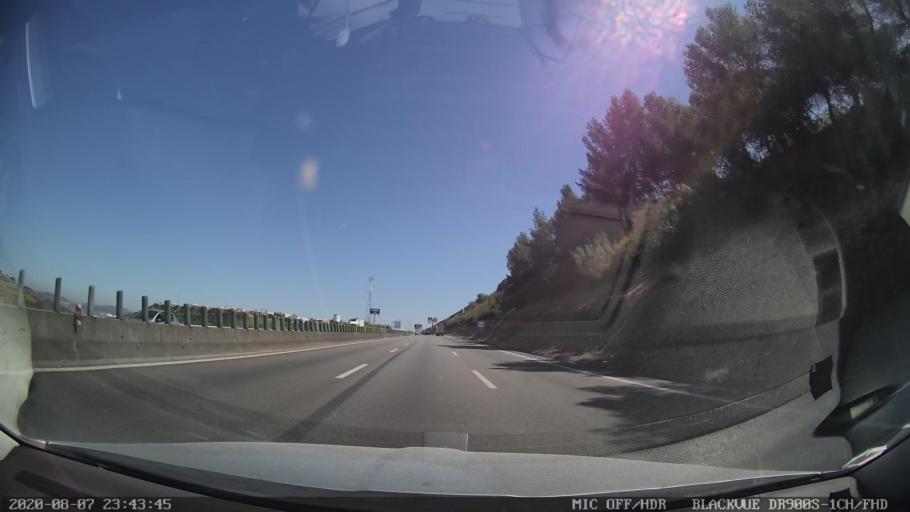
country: PT
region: Lisbon
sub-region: Loures
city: Bobadela
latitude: 38.8033
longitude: -9.1020
